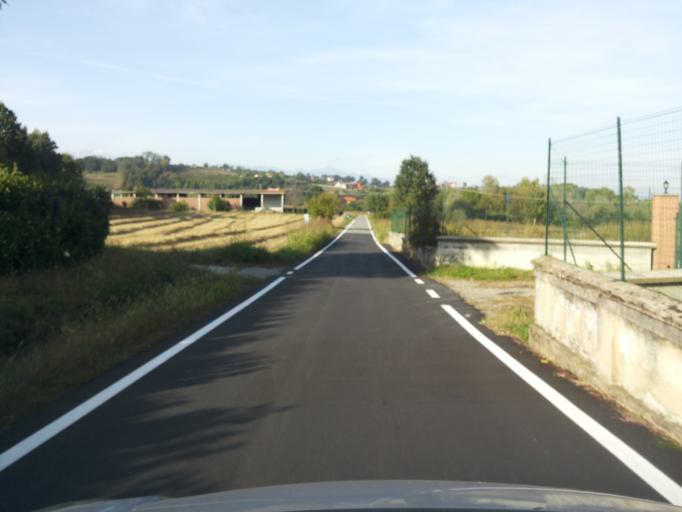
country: IT
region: Piedmont
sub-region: Provincia di Biella
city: Dorzano
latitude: 45.4330
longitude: 8.0956
